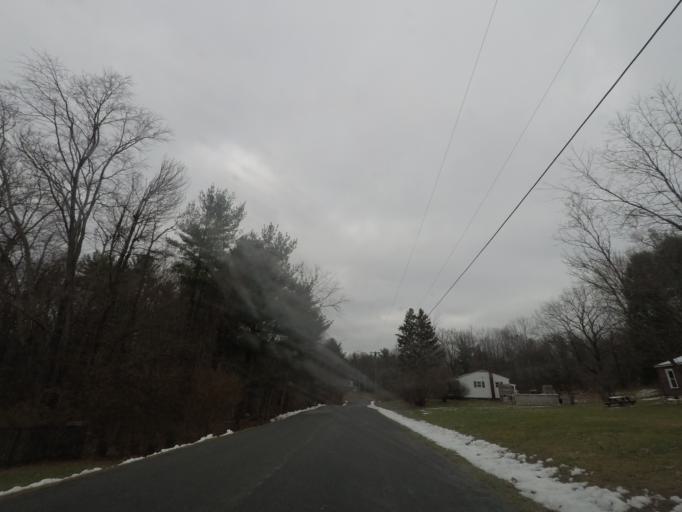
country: US
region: New York
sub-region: Rensselaer County
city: East Greenbush
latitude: 42.5887
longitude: -73.6448
